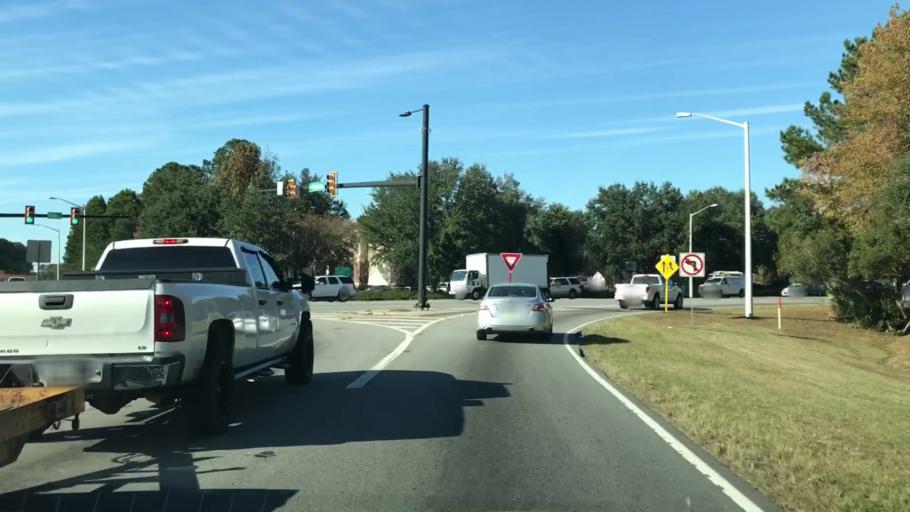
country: US
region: South Carolina
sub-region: Beaufort County
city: Bluffton
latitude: 32.2944
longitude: -80.9362
